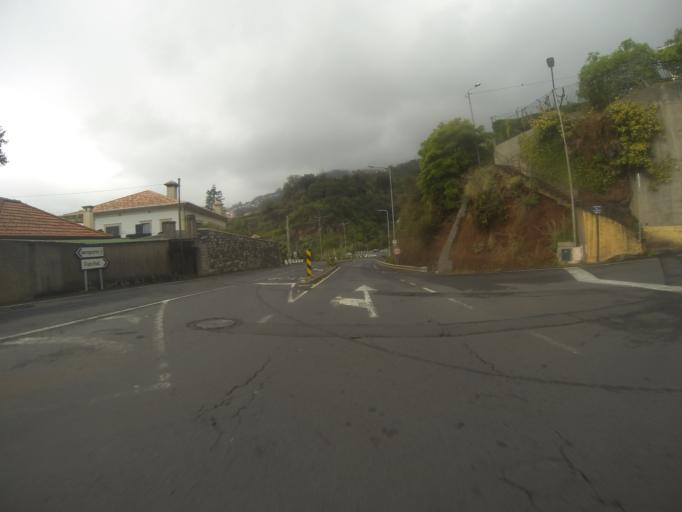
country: PT
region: Madeira
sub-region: Funchal
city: Nossa Senhora do Monte
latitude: 32.6547
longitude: -16.8781
